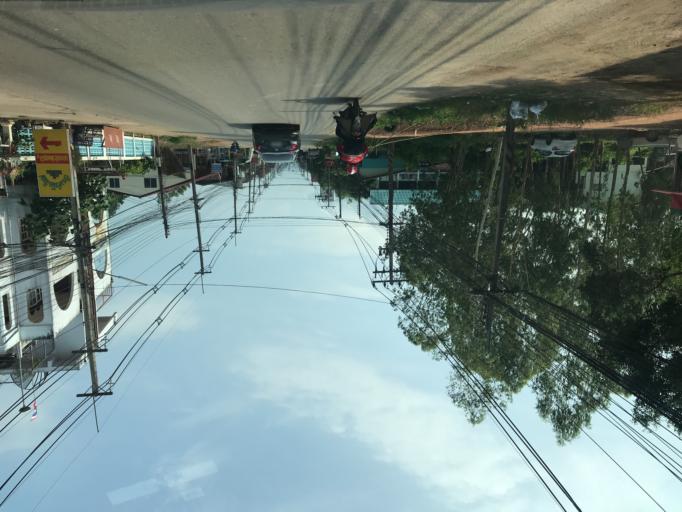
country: TH
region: Phayao
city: Chiang Kham
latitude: 19.5332
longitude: 100.3006
